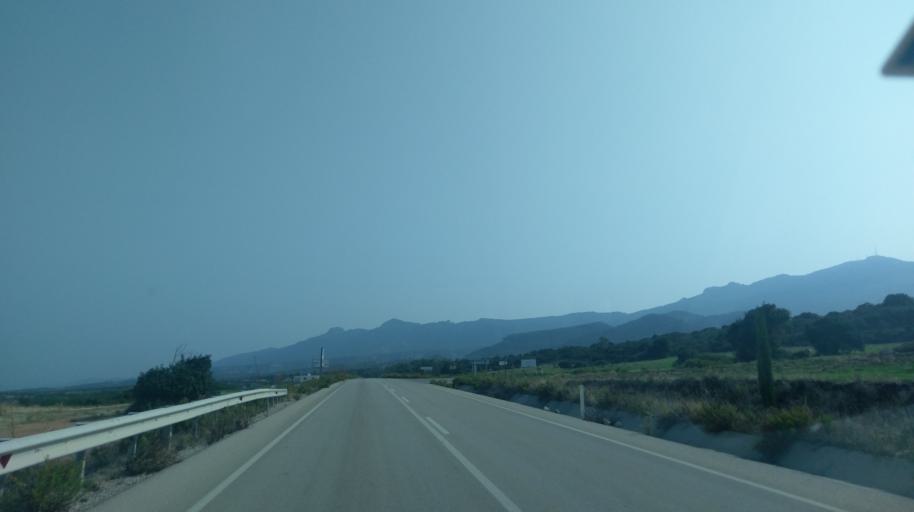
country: CY
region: Ammochostos
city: Trikomo
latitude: 35.4118
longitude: 33.8456
